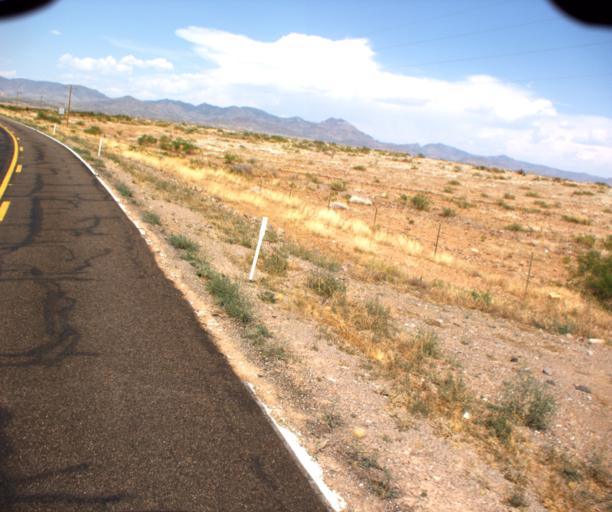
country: US
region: Arizona
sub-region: Greenlee County
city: Clifton
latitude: 32.9494
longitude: -109.2268
